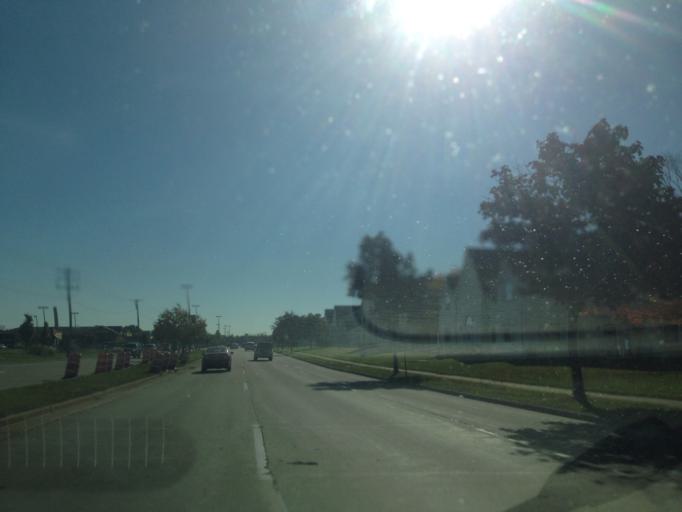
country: US
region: Wisconsin
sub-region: Milwaukee County
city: West Milwaukee
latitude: 43.0100
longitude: -87.9678
